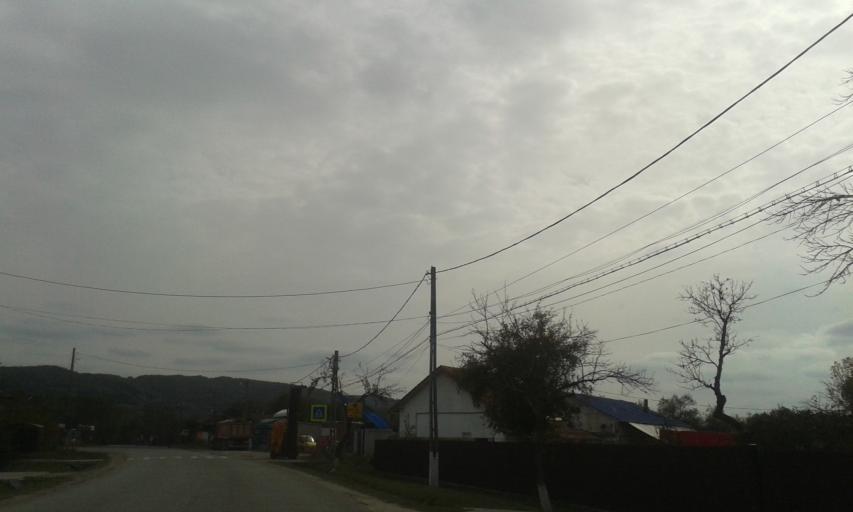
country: RO
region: Gorj
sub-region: Comuna Hurezani
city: Hurezani
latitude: 44.8175
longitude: 23.6525
